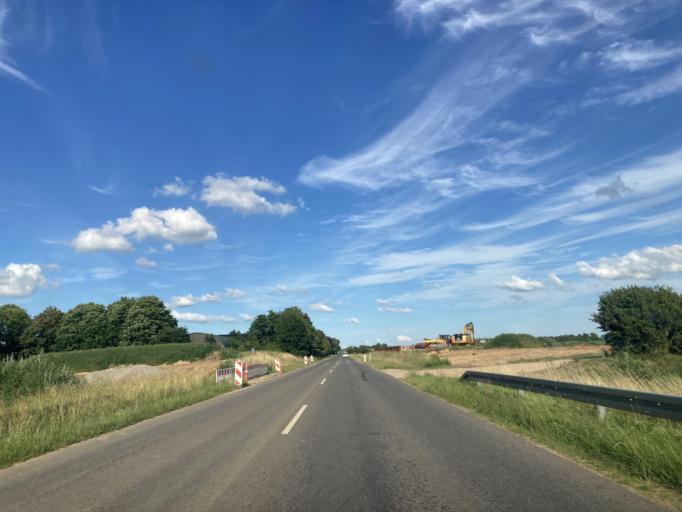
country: DK
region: South Denmark
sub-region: Kolding Kommune
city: Lunderskov
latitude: 55.4851
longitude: 9.3286
